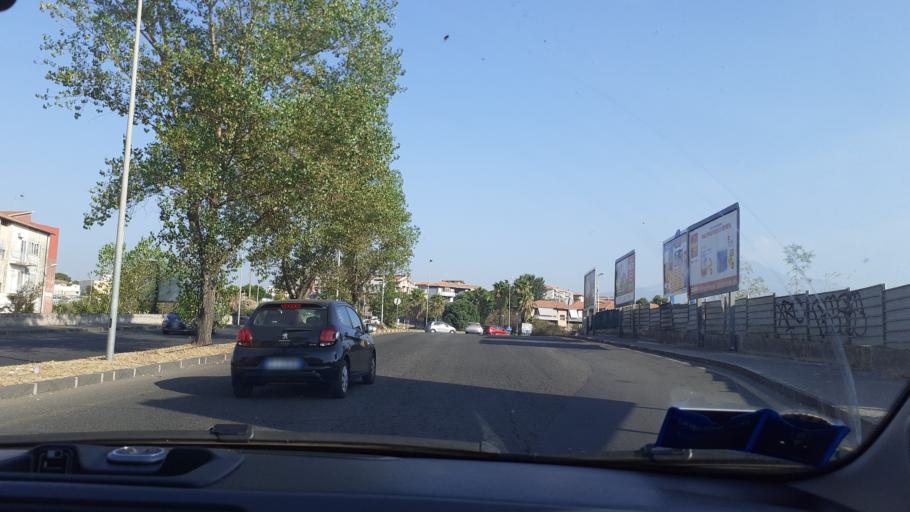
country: IT
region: Sicily
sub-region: Catania
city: Misterbianco
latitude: 37.5157
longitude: 15.0527
